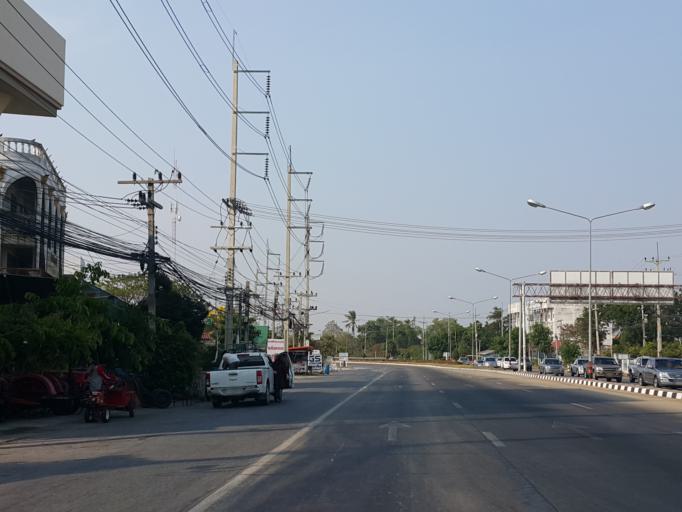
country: TH
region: Suphan Buri
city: Doembang Nangbuat
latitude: 14.8094
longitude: 100.1176
